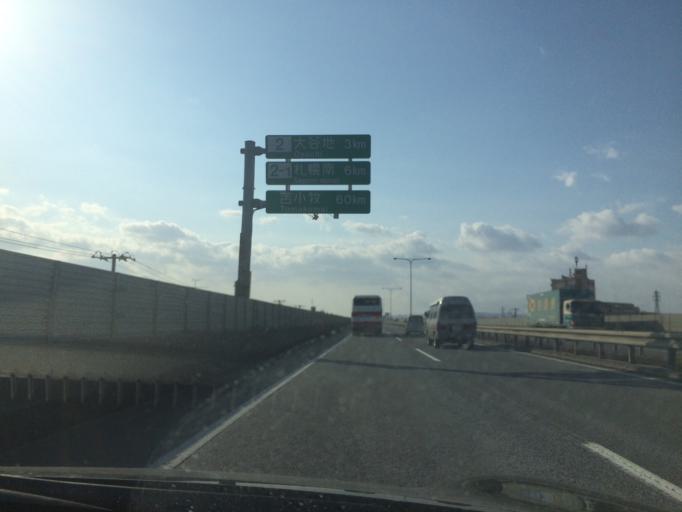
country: JP
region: Hokkaido
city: Sapporo
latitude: 43.0652
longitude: 141.4236
